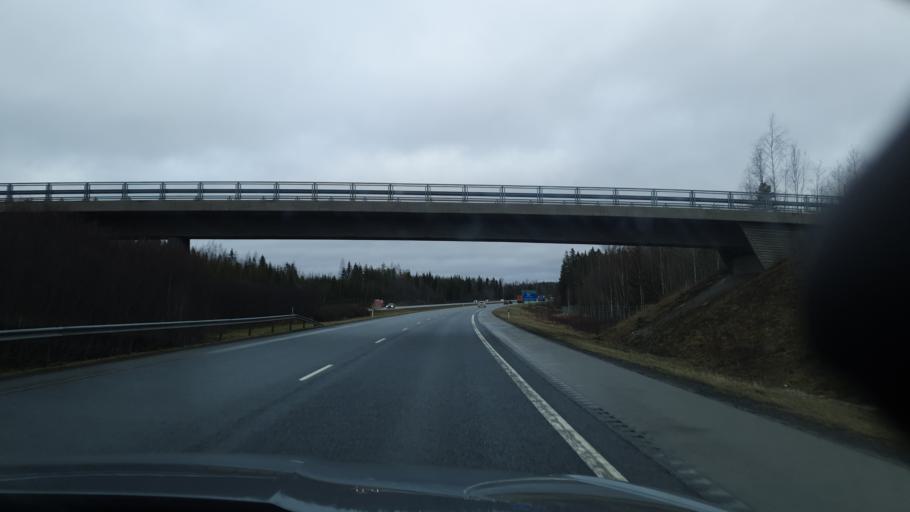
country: FI
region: Pirkanmaa
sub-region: Tampere
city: Lempaeaelae
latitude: 61.2804
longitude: 23.8097
